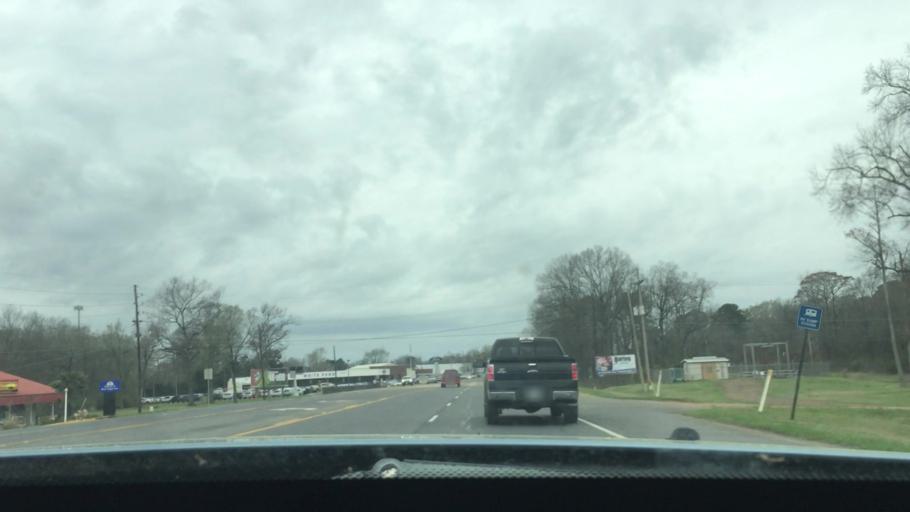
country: US
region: Louisiana
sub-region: Franklin Parish
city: Winnsboro
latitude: 32.1542
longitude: -91.7104
